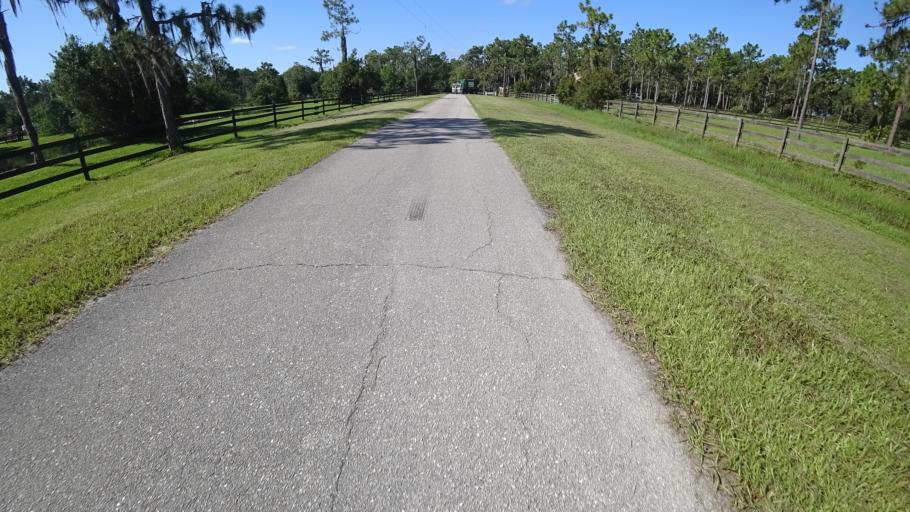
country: US
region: Florida
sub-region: Sarasota County
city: The Meadows
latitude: 27.4159
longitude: -82.3307
